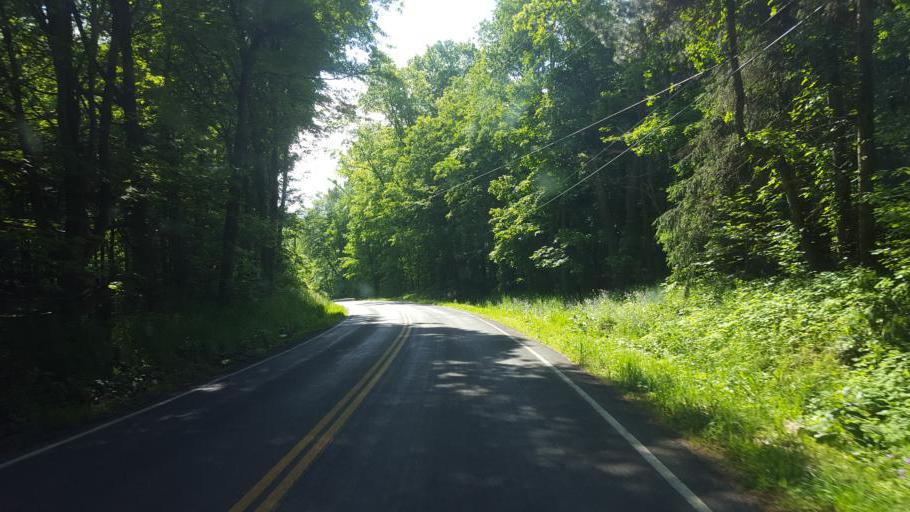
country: US
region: Ohio
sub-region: Medina County
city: Seville
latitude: 41.0574
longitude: -81.8060
